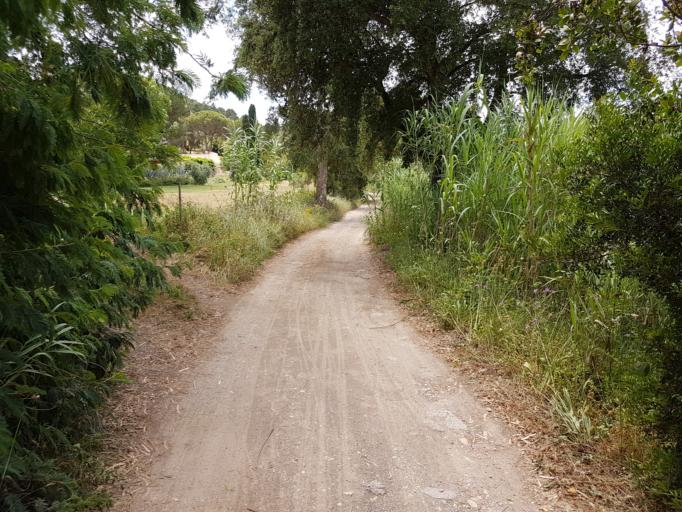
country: IT
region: Tuscany
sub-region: Provincia di Livorno
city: Portoferraio
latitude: 42.7887
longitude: 10.3491
